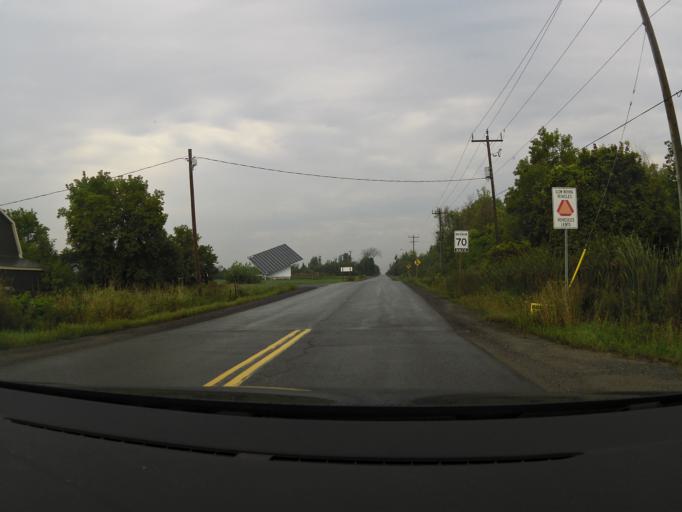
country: CA
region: Ontario
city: Carleton Place
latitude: 45.1737
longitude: -76.0532
